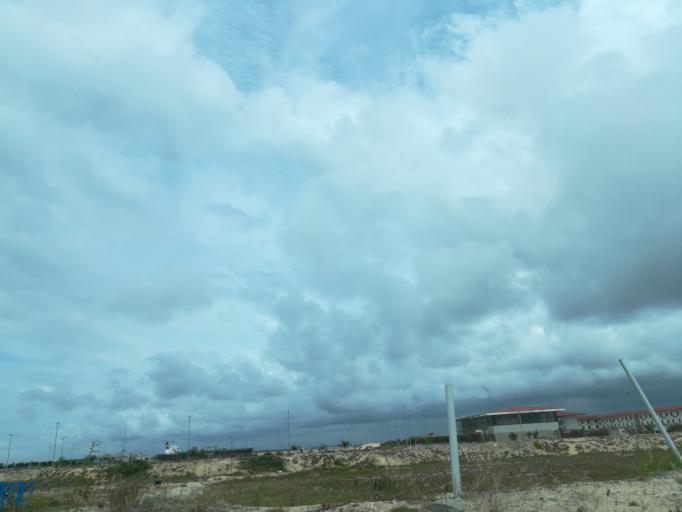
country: NG
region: Lagos
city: Lagos
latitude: 6.4110
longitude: 3.4077
